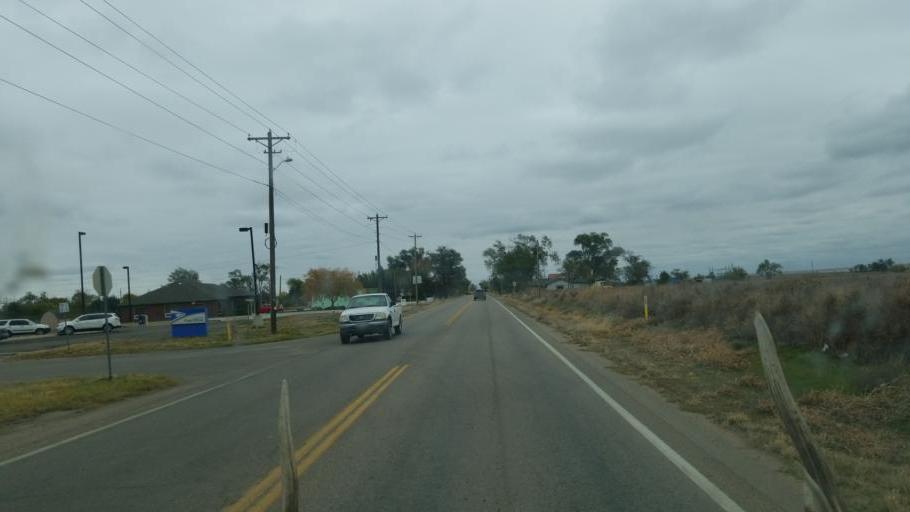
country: US
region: Colorado
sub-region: Crowley County
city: Ordway
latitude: 38.2146
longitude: -103.7556
